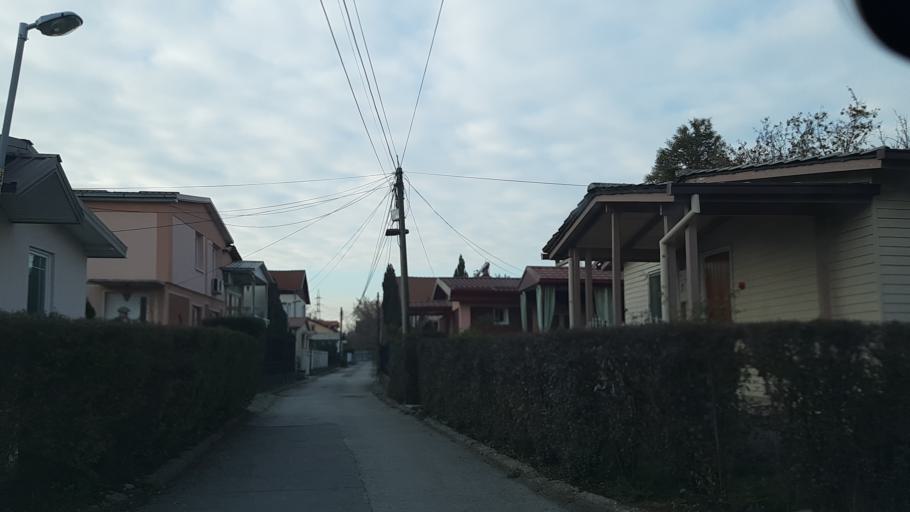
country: MK
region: Kisela Voda
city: Usje
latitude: 41.9765
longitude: 21.4521
